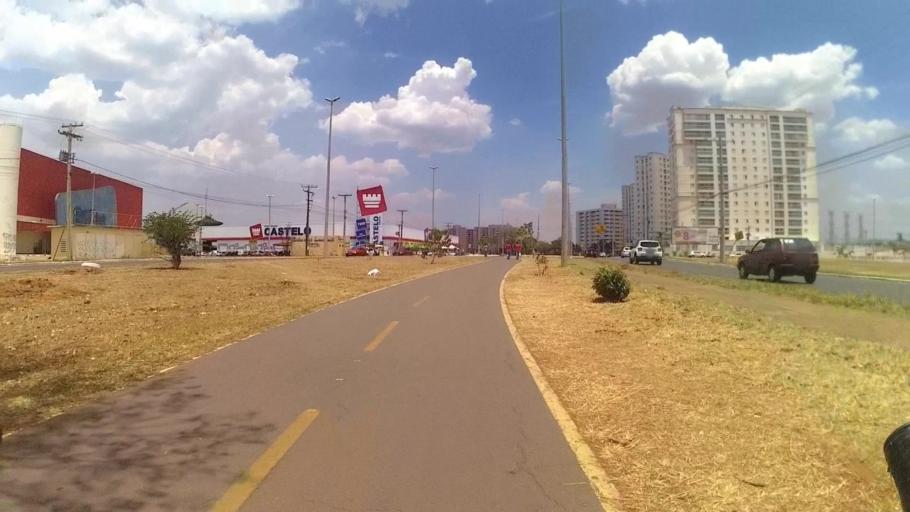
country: BR
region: Federal District
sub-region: Brasilia
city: Brasilia
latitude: -15.8766
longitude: -48.0829
